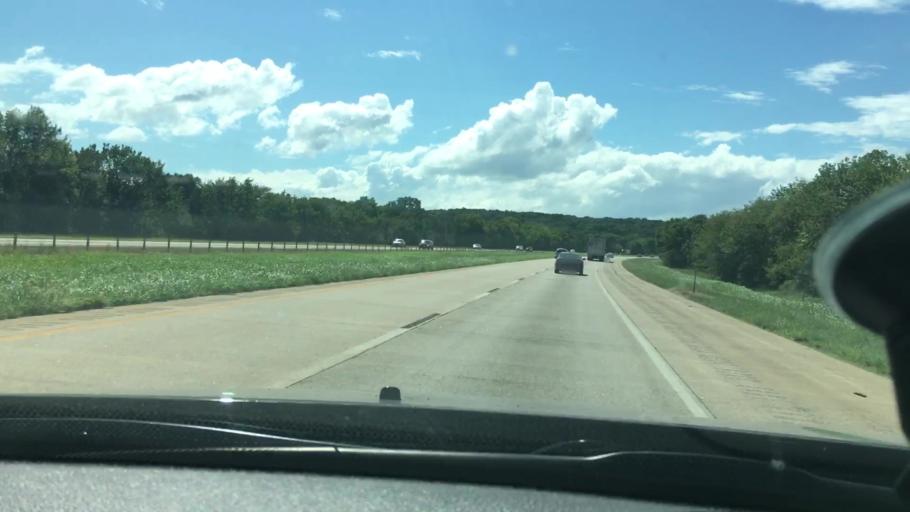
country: US
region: Oklahoma
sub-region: Sequoyah County
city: Vian
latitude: 35.4897
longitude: -95.0303
